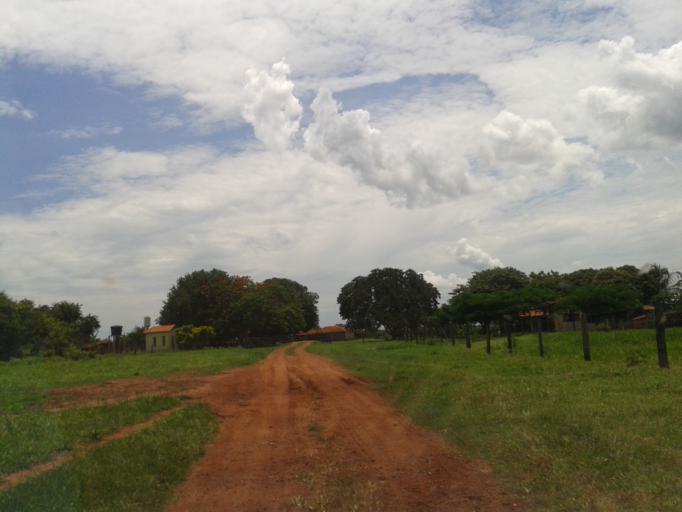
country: BR
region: Minas Gerais
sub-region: Santa Vitoria
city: Santa Vitoria
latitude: -19.1513
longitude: -50.6234
